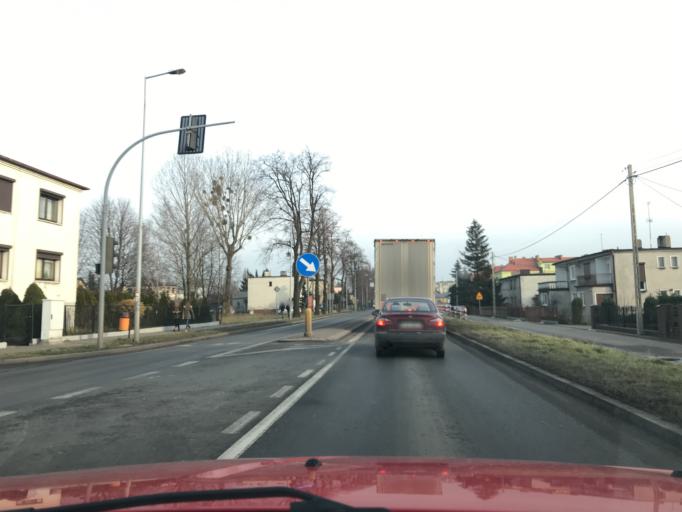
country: PL
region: Greater Poland Voivodeship
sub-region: Powiat pleszewski
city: Pleszew
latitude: 51.8977
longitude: 17.7717
